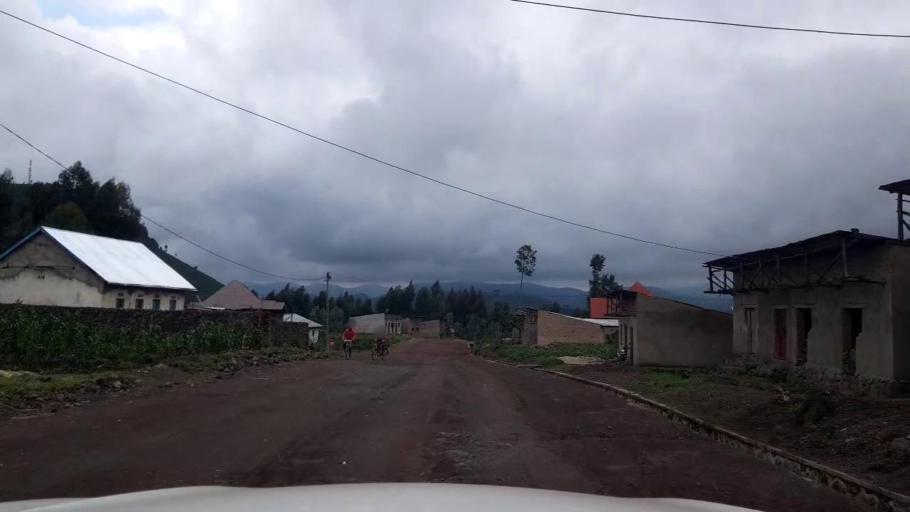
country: RW
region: Northern Province
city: Musanze
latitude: -1.5990
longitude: 29.4523
